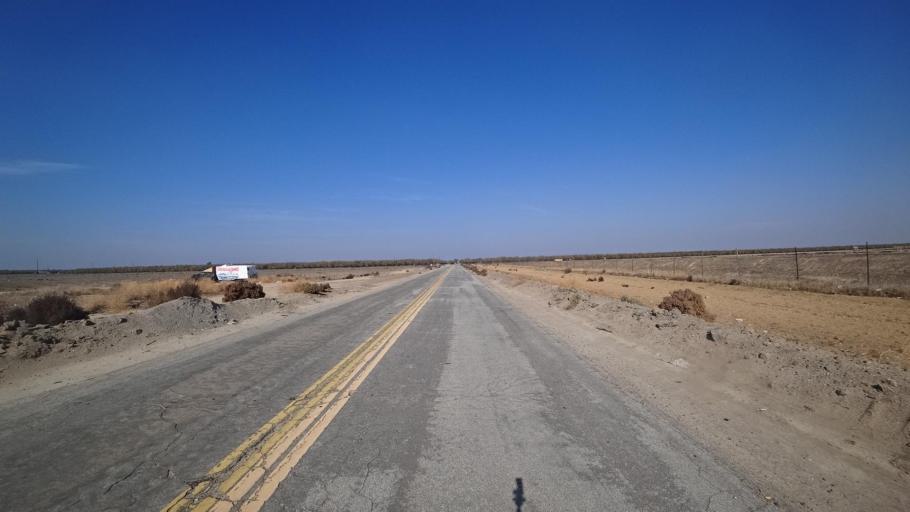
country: US
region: California
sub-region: Kern County
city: Shafter
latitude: 35.5336
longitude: -119.1868
